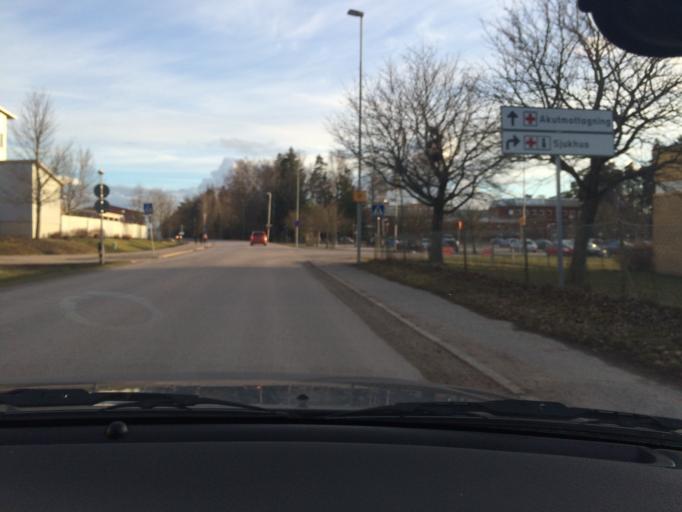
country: SE
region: Vaestmanland
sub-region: Vasteras
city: Vasteras
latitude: 59.6205
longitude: 16.5887
